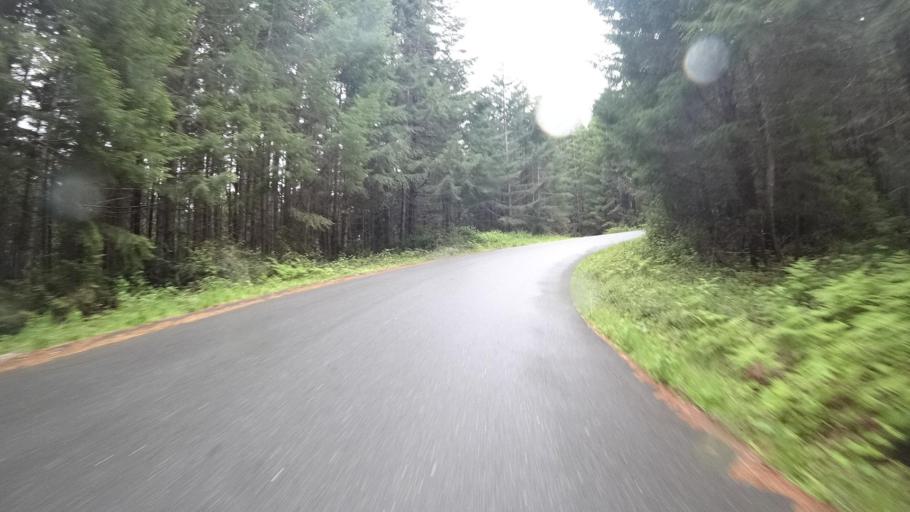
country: US
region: California
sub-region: Humboldt County
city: Willow Creek
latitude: 41.1992
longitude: -123.7619
